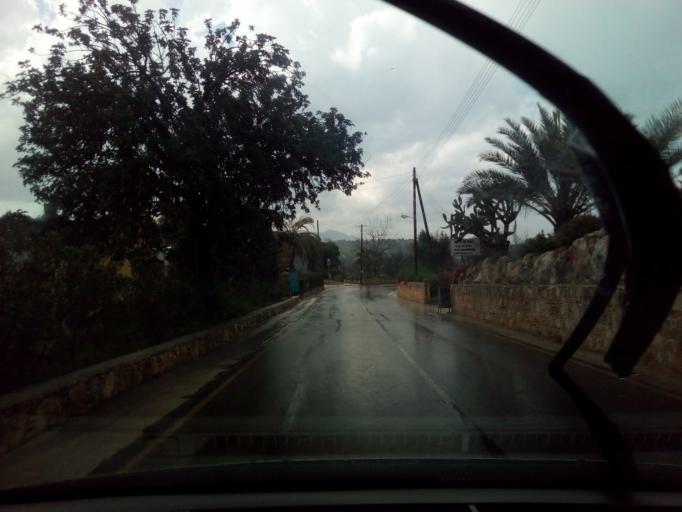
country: CY
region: Pafos
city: Polis
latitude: 35.0000
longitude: 32.4701
